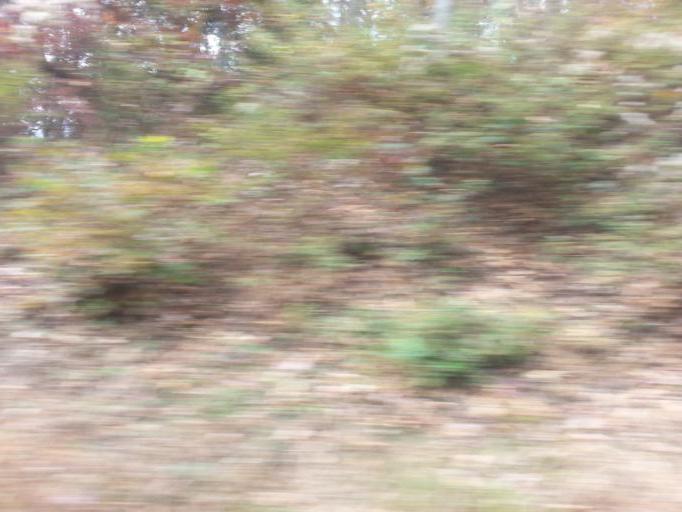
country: US
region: Virginia
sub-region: City of Galax
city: Galax
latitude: 36.5516
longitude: -80.9132
